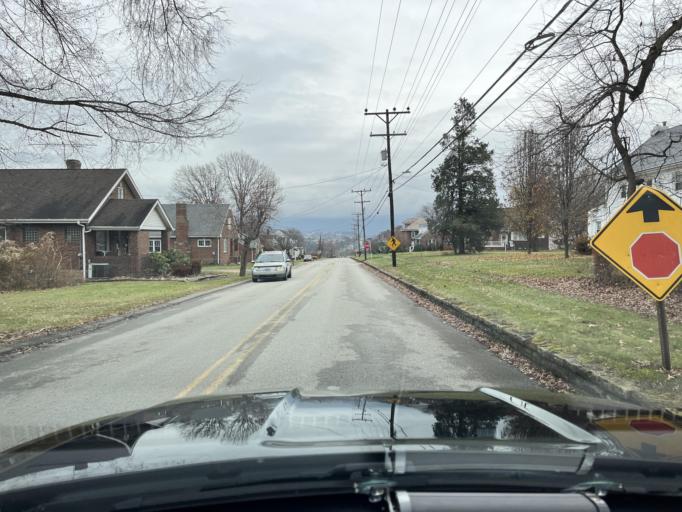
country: US
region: Pennsylvania
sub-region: Fayette County
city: South Uniontown
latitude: 39.8957
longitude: -79.7496
